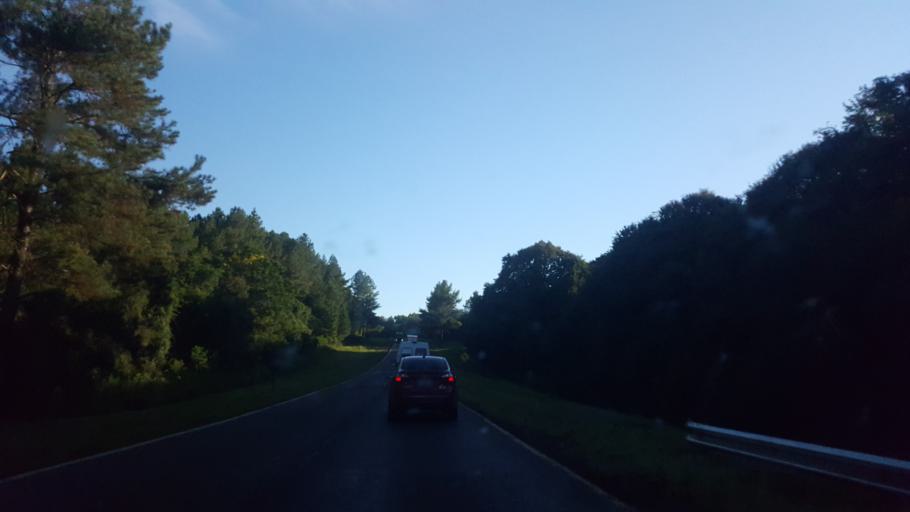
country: AR
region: Misiones
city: El Alcazar
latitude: -26.7619
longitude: -54.8879
